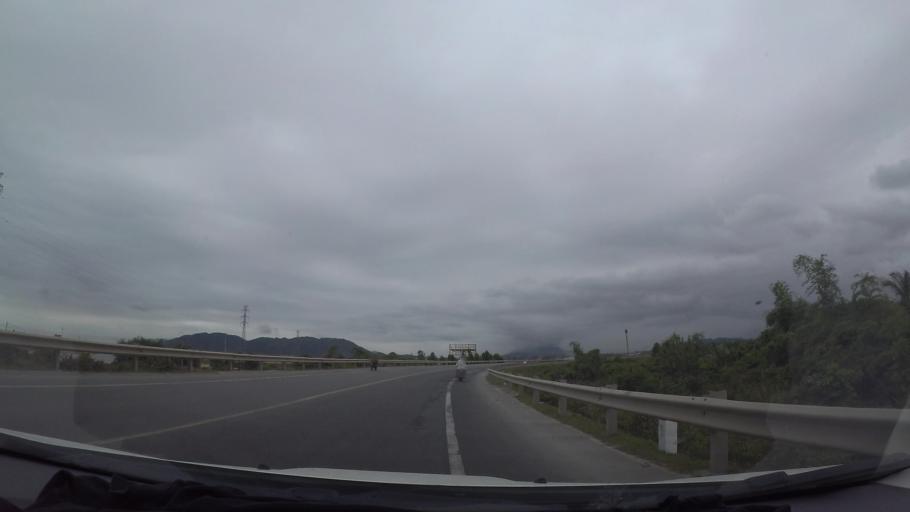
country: VN
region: Da Nang
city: Lien Chieu
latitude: 16.1098
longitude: 108.1047
